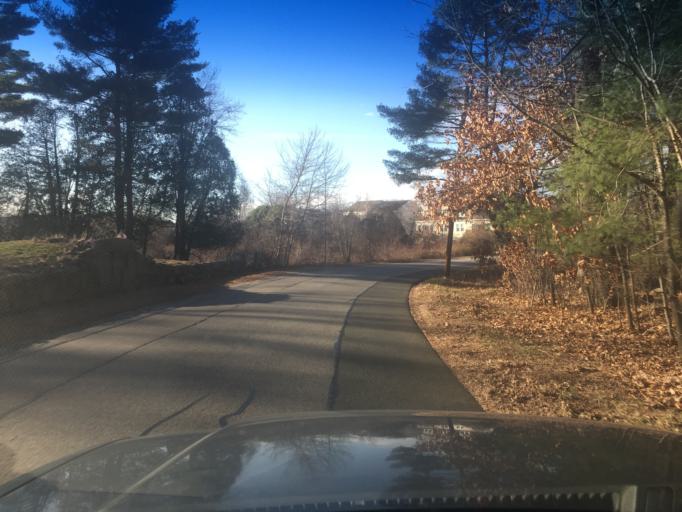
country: US
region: Massachusetts
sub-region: Middlesex County
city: Hopkinton
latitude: 42.2314
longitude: -71.4869
